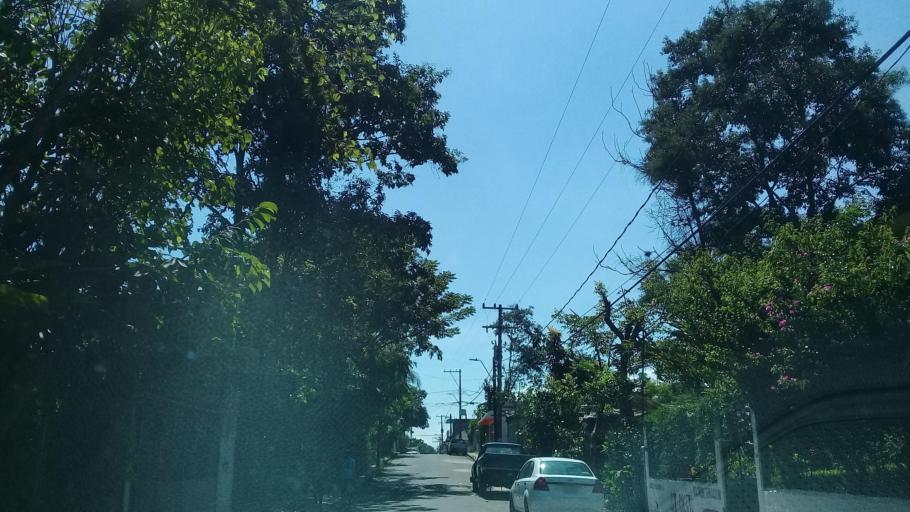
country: MX
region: Veracruz
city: Amatlan de los Reyes
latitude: 18.8499
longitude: -96.9170
